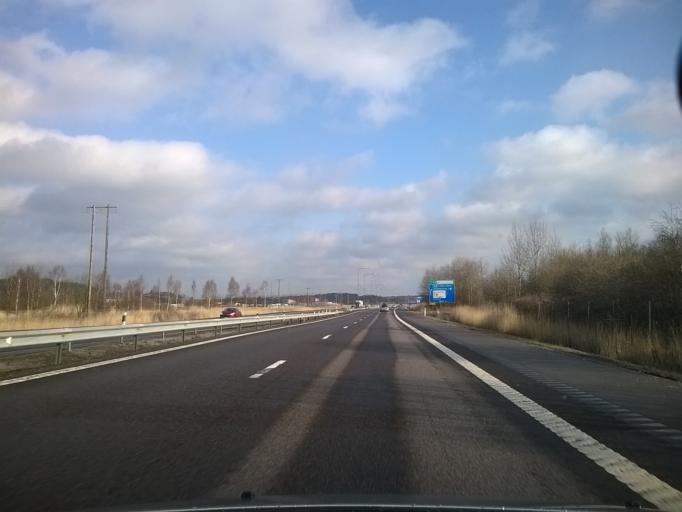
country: SE
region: Vaestra Goetaland
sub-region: Stenungsunds Kommun
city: Stora Hoga
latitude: 58.0152
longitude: 11.8436
